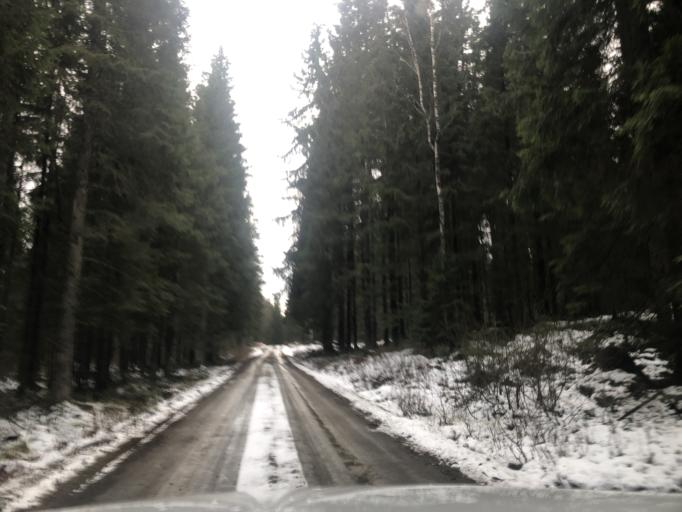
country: SE
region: Vaestra Goetaland
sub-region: Ulricehamns Kommun
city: Ulricehamn
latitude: 57.7861
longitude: 13.4822
